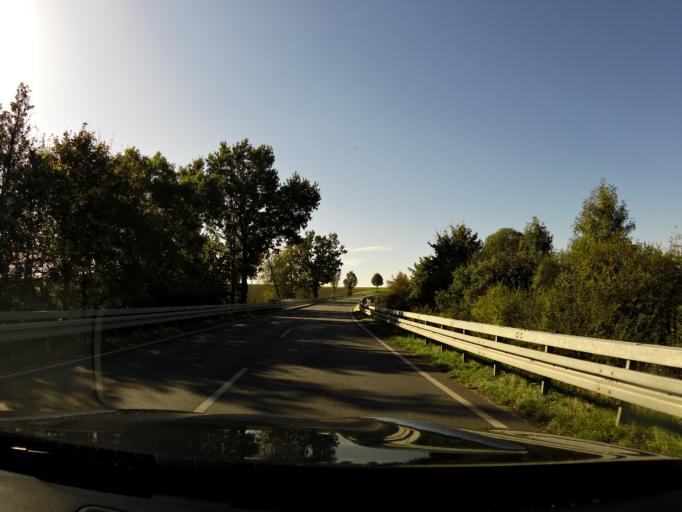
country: DE
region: Bavaria
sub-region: Lower Bavaria
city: Altfraunhofen
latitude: 48.4500
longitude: 12.1497
